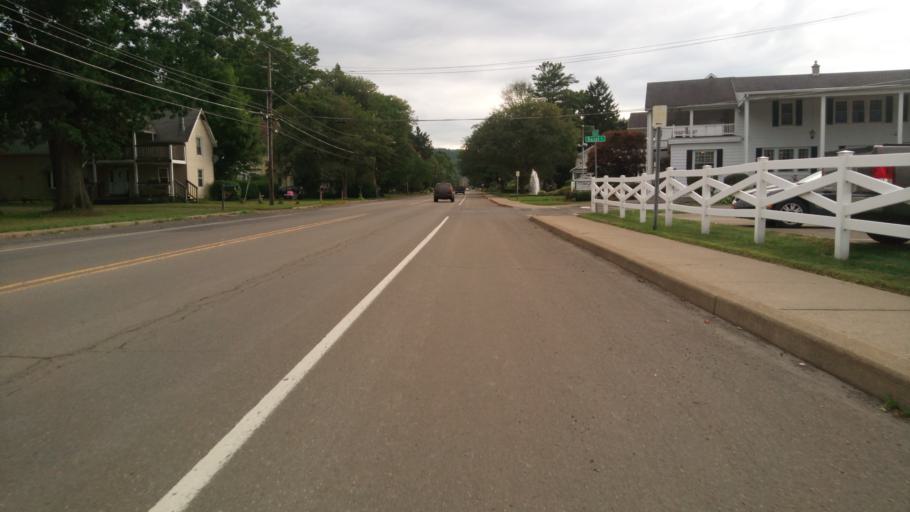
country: US
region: New York
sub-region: Chemung County
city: Southport
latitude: 42.0596
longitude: -76.8123
